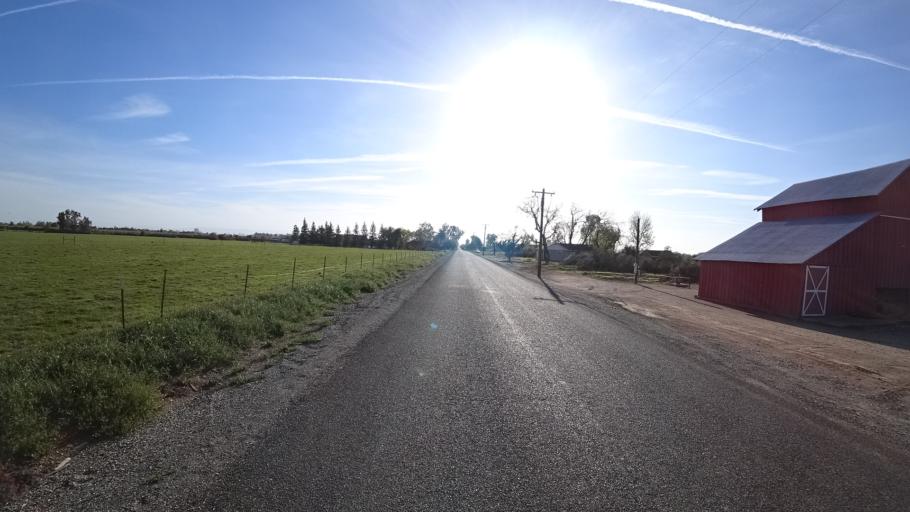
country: US
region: California
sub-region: Glenn County
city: Orland
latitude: 39.7261
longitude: -122.2294
